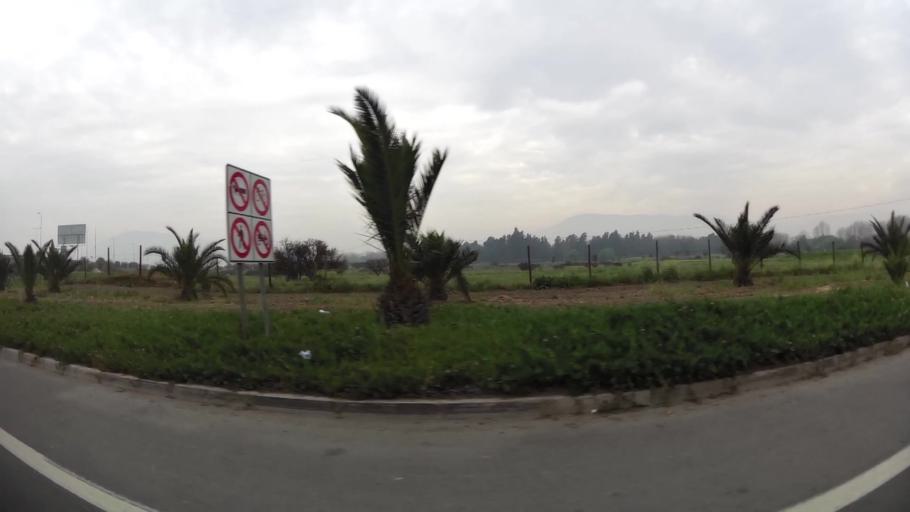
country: CL
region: Santiago Metropolitan
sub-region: Provincia de Santiago
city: Lo Prado
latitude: -33.4179
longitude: -70.7927
